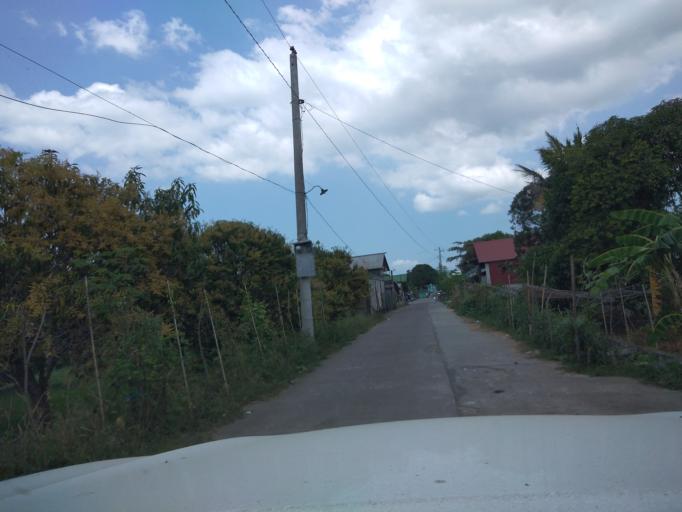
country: PH
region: Central Luzon
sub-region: Province of Pampanga
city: Lourdes
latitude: 15.0140
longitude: 120.8663
